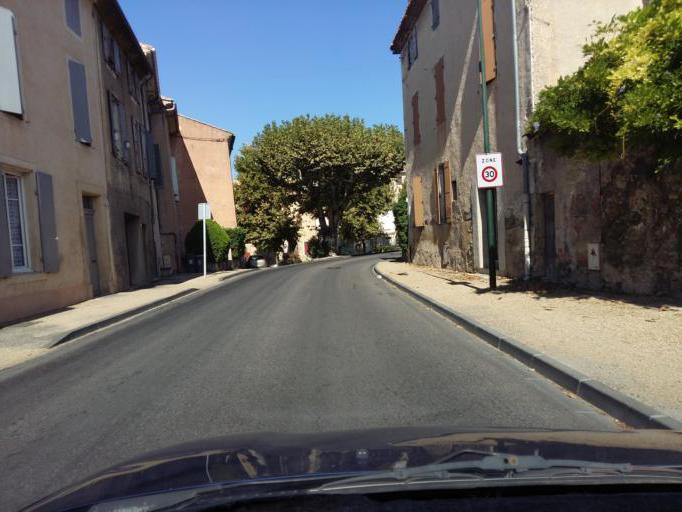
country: FR
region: Provence-Alpes-Cote d'Azur
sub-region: Departement du Vaucluse
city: Mazan
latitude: 44.0556
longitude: 5.1311
